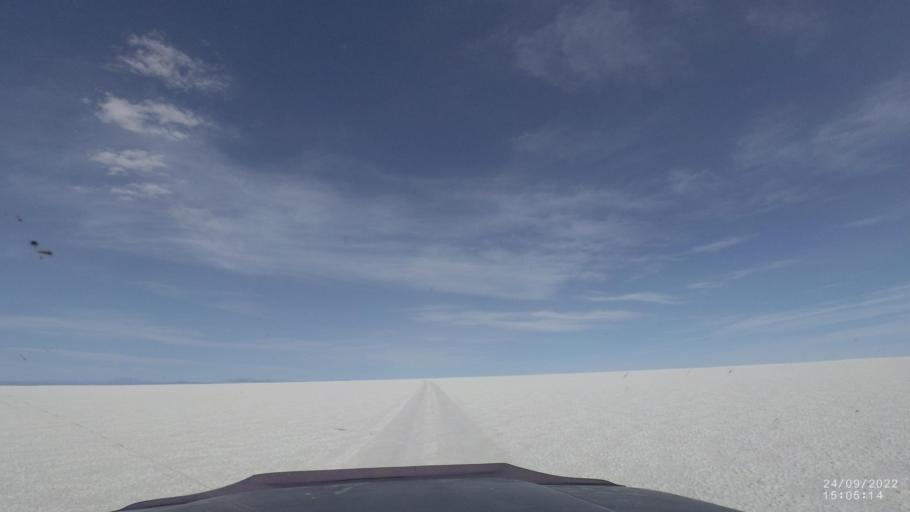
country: BO
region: Potosi
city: Colchani
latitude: -19.9046
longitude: -67.5191
